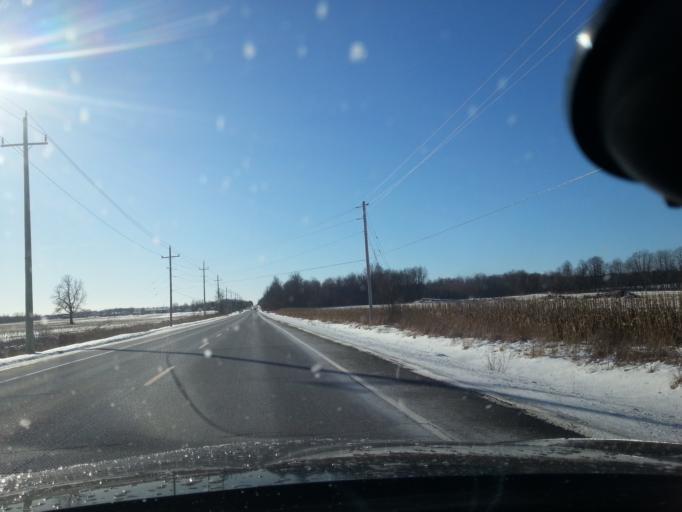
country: CA
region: Ontario
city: Ottawa
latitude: 45.2942
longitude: -75.5361
